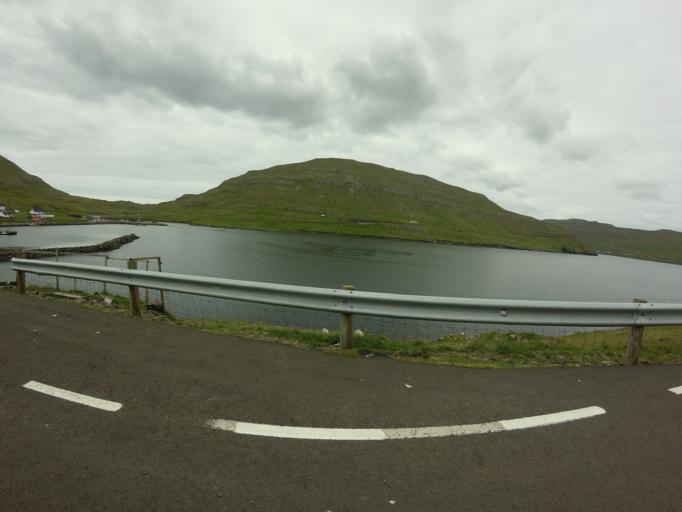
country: FO
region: Suduroy
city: Vagur
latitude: 61.4461
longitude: -6.7666
